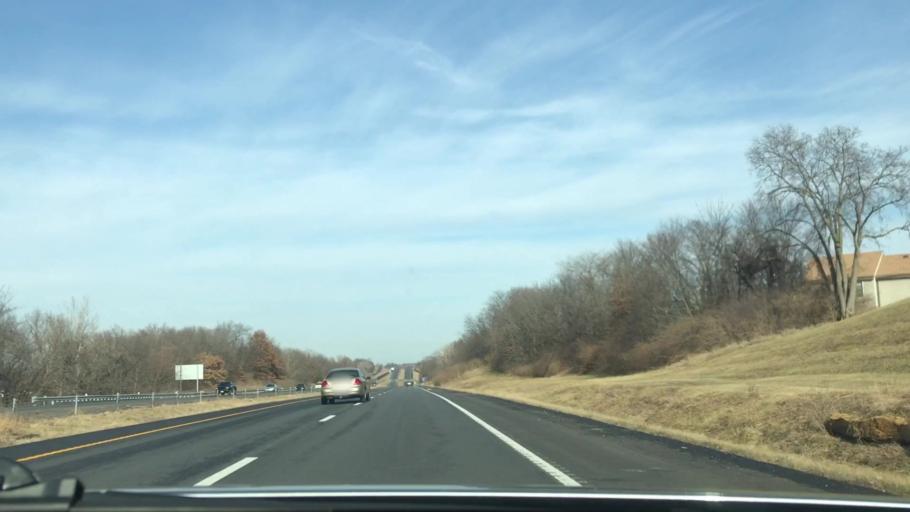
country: US
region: Missouri
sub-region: Clay County
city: Gladstone
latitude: 39.2068
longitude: -94.5896
